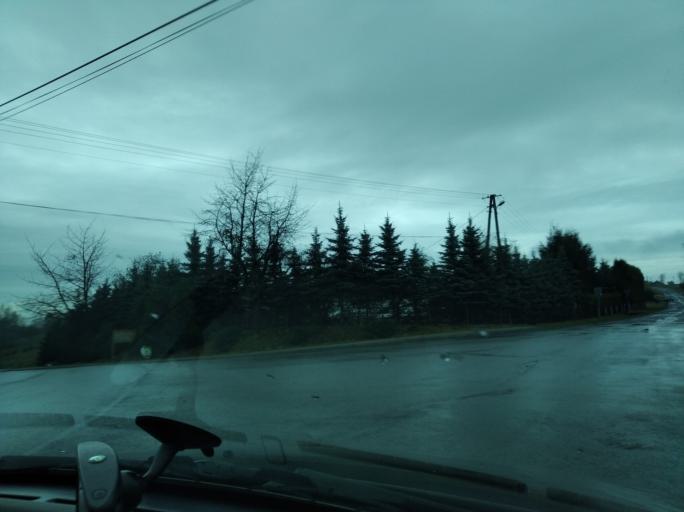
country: PL
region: Subcarpathian Voivodeship
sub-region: Powiat rzeszowski
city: Tyczyn
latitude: 49.9268
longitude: 22.0281
